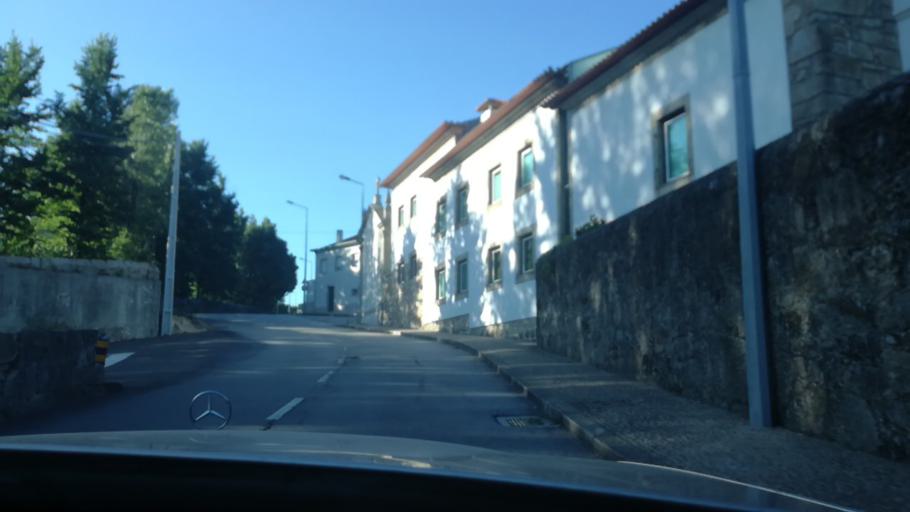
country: PT
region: Porto
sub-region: Maia
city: Leca do Bailio
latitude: 41.2203
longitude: -8.6236
